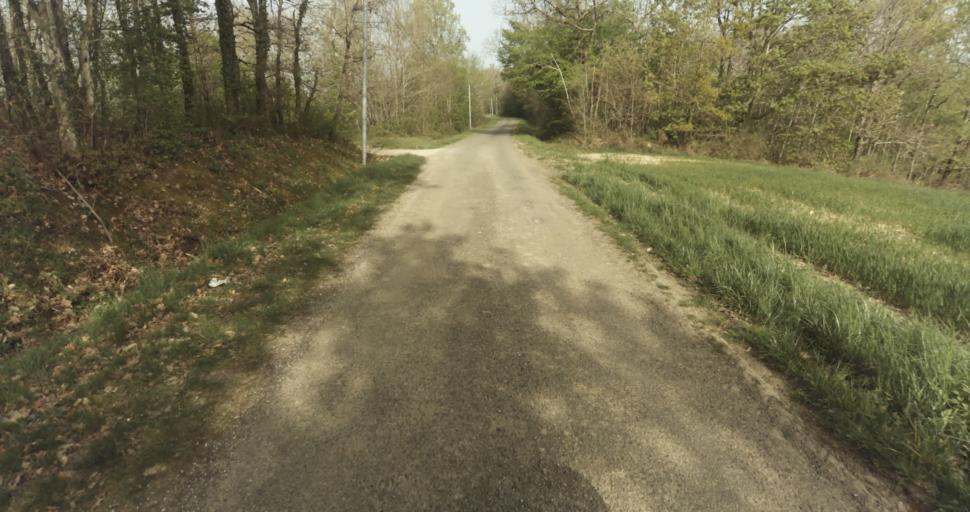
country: FR
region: Midi-Pyrenees
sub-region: Departement du Tarn-et-Garonne
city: Moissac
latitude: 44.1604
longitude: 1.0585
